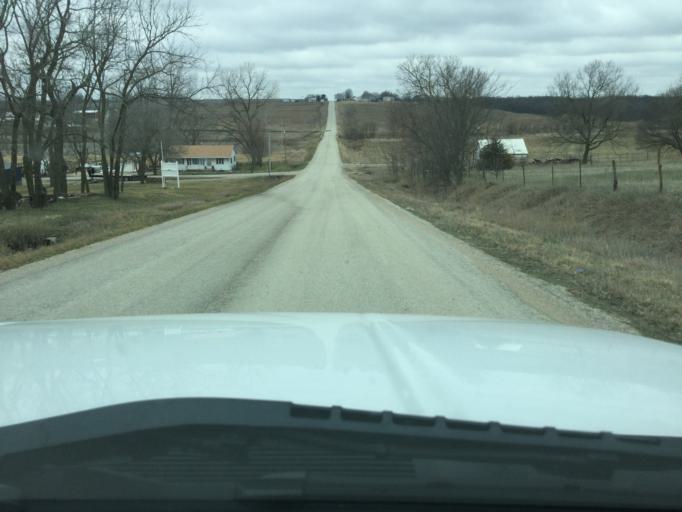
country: US
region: Kansas
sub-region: Nemaha County
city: Seneca
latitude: 39.7399
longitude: -96.0031
